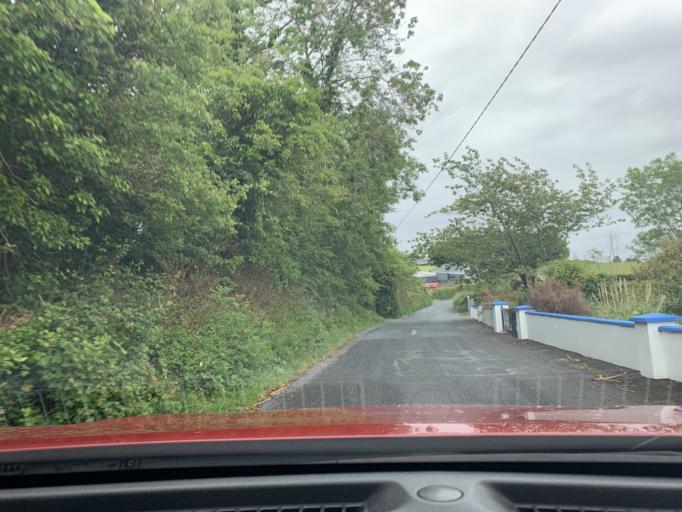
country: IE
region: Connaught
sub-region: Sligo
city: Sligo
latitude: 54.3113
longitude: -8.4755
